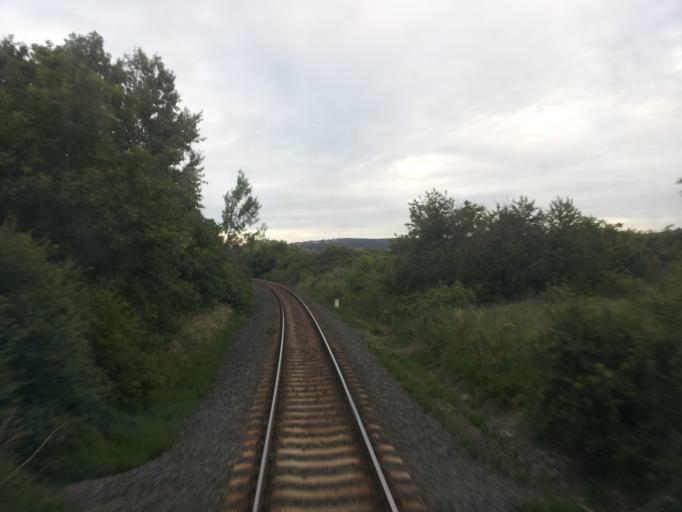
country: HU
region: Veszprem
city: Balatonalmadi
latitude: 47.0536
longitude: 18.0276
